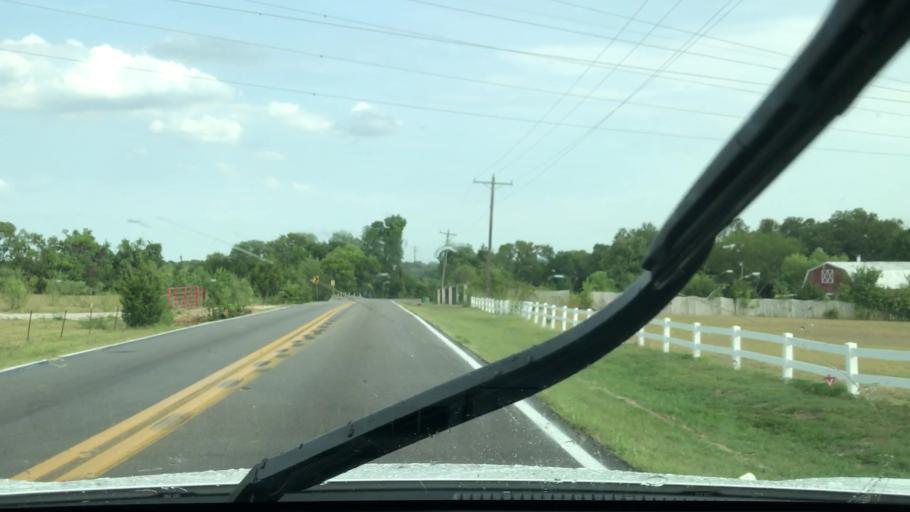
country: US
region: Texas
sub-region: Collin County
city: Wylie
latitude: 32.9709
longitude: -96.5241
